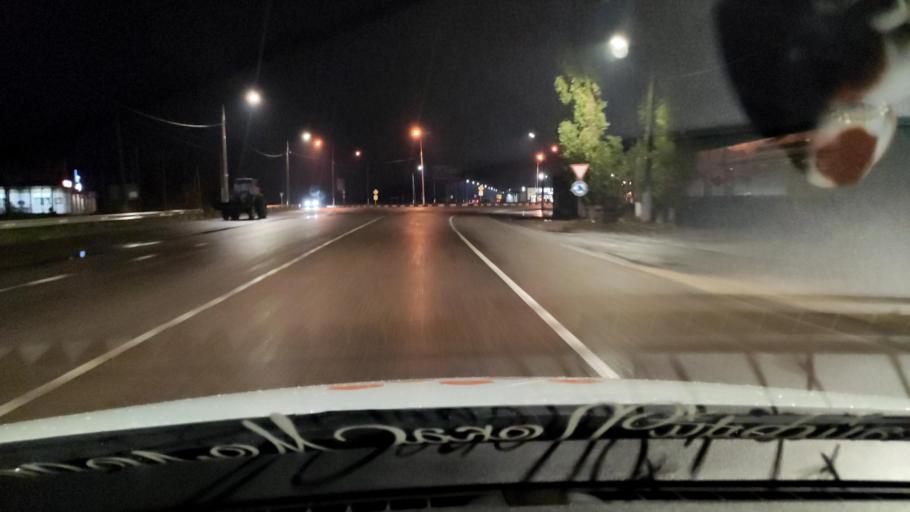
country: RU
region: Voronezj
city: Semiluki
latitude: 51.7245
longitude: 39.0346
